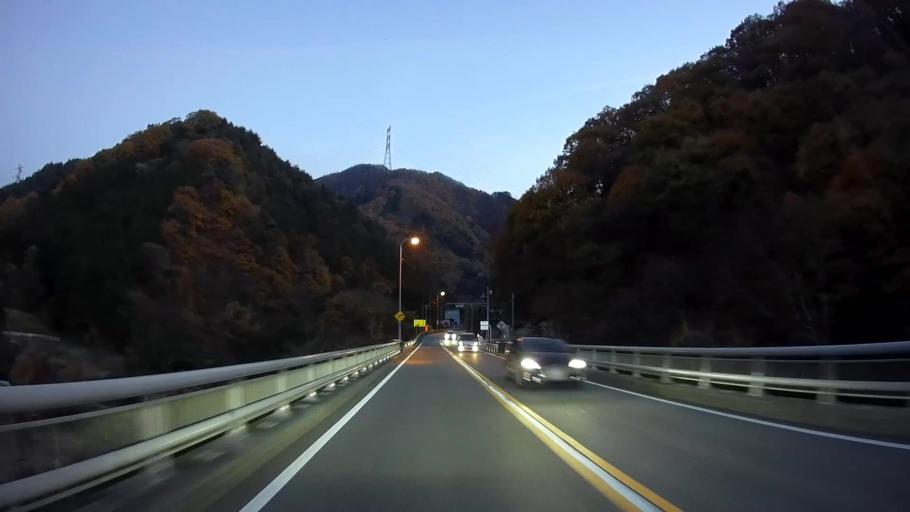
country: JP
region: Yamanashi
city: Enzan
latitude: 35.6387
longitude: 138.7911
